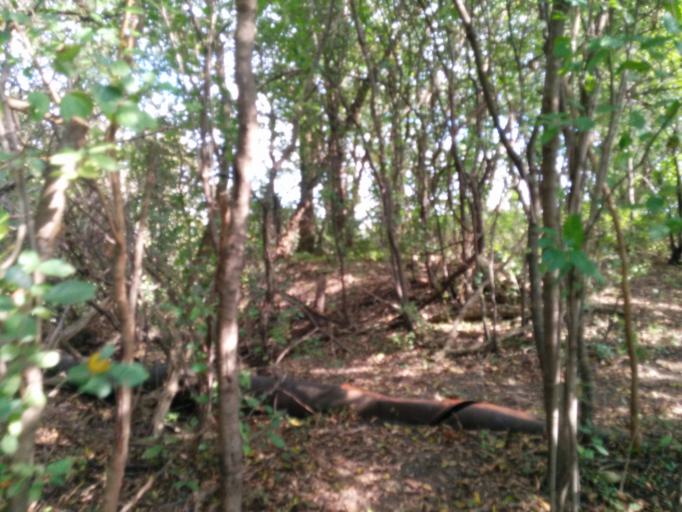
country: US
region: Illinois
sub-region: DuPage County
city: Carol Stream
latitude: 41.9386
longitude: -88.1813
